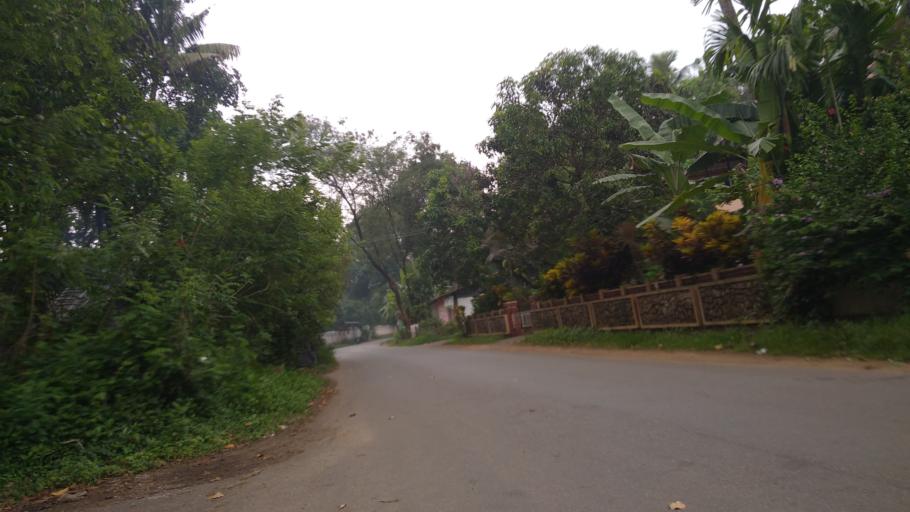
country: IN
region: Kerala
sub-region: Ernakulam
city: Perumbavoor
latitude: 10.0871
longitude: 76.5059
